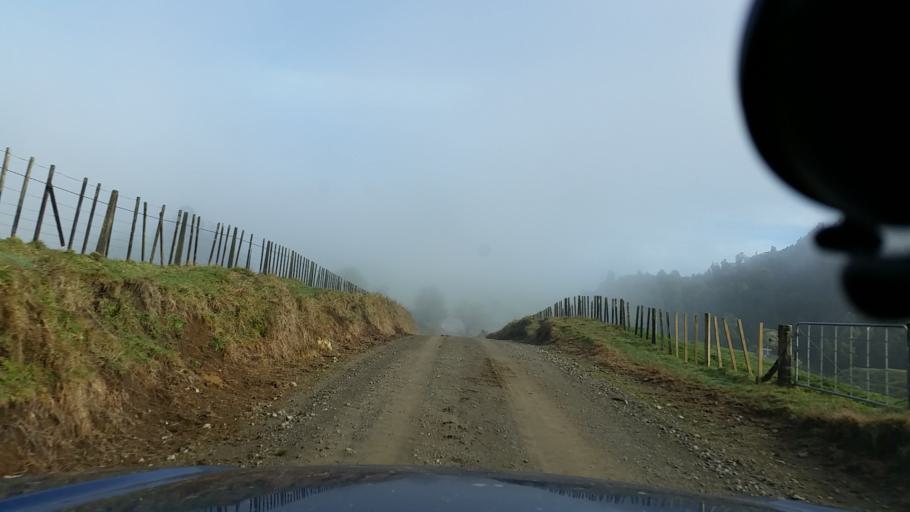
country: NZ
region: Taranaki
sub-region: New Plymouth District
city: Waitara
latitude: -38.9786
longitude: 174.7572
